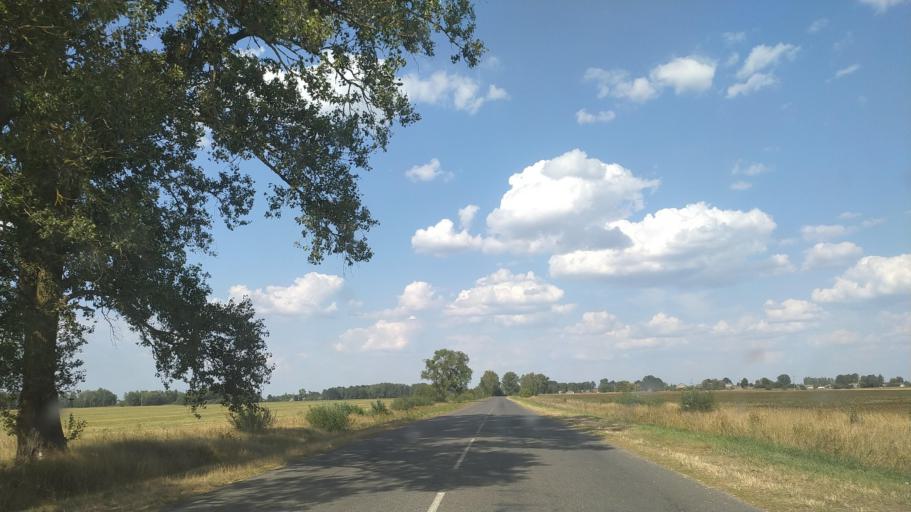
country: BY
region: Brest
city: Drahichyn
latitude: 52.1264
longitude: 25.1179
